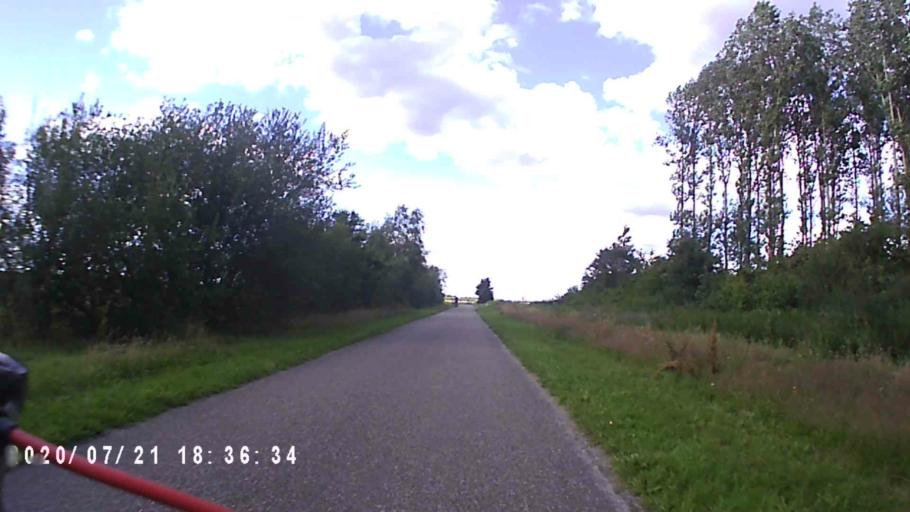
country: NL
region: Groningen
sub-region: Gemeente Hoogezand-Sappemeer
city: Hoogezand
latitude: 53.1943
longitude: 6.7426
